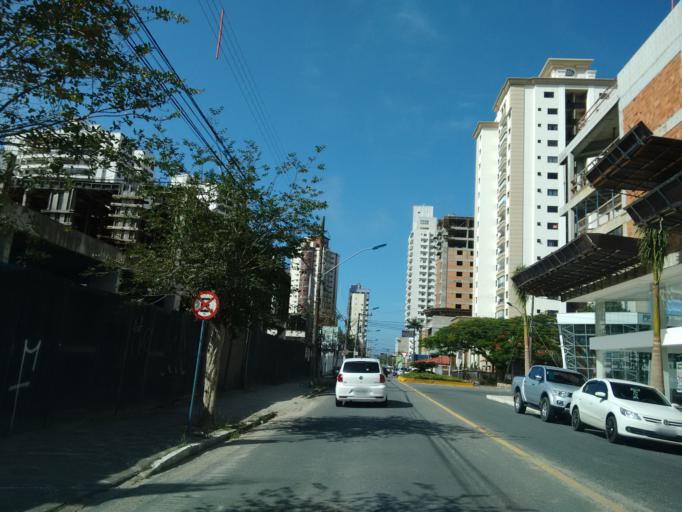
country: BR
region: Santa Catarina
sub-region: Itajai
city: Itajai
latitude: -26.9226
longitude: -48.6518
